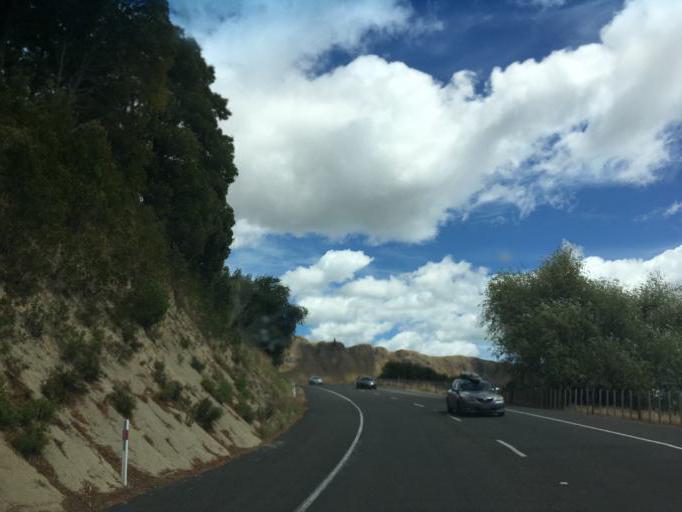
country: NZ
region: Hawke's Bay
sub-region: Hastings District
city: Hastings
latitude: -39.7012
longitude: 176.9297
